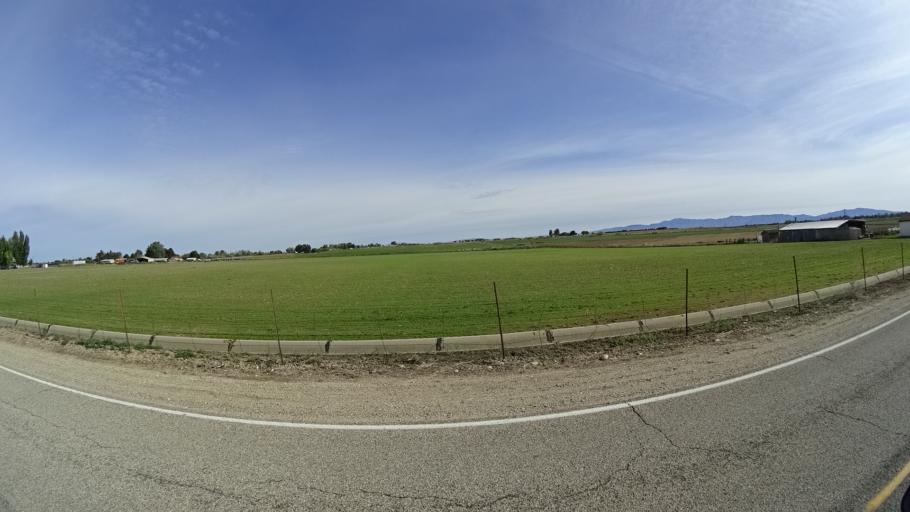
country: US
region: Idaho
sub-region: Ada County
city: Kuna
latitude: 43.4735
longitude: -116.3506
